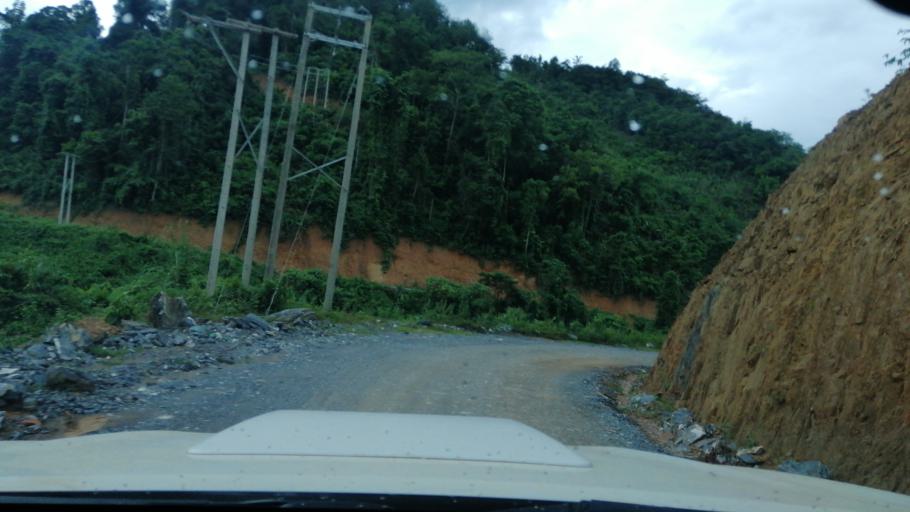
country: LA
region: Xiagnabouli
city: Sainyabuli
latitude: 19.1832
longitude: 101.7960
